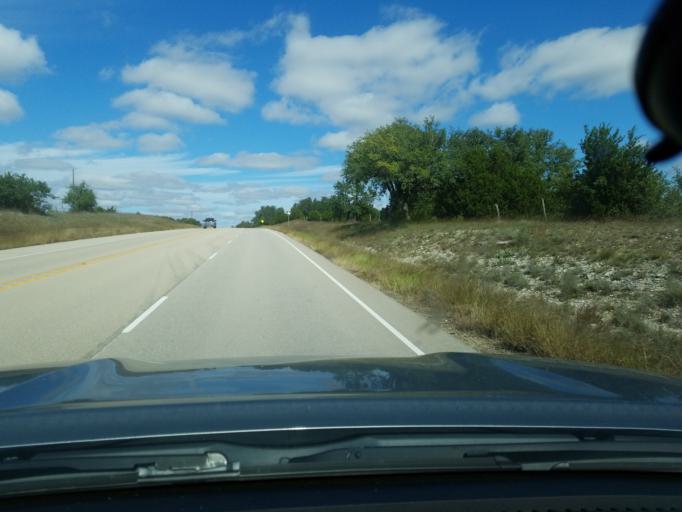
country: US
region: Texas
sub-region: Hamilton County
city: Hamilton
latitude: 31.5874
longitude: -98.1567
